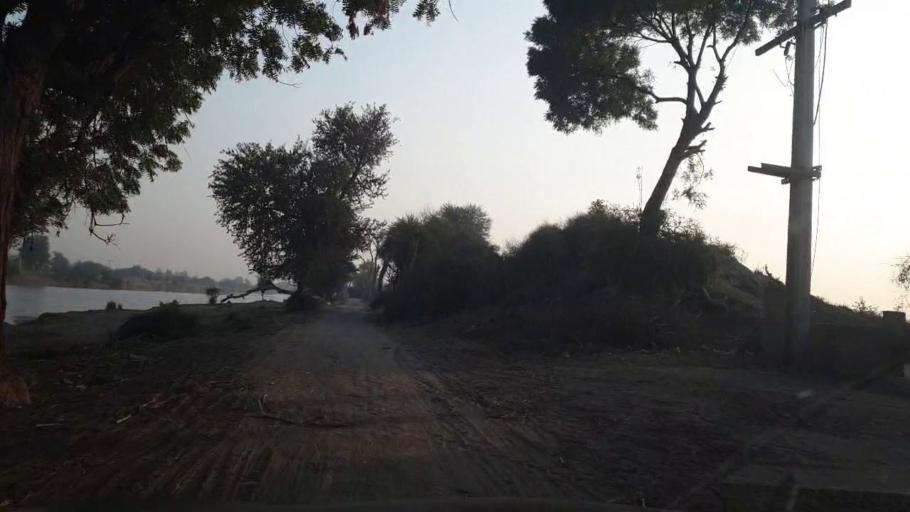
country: PK
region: Sindh
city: Ubauro
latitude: 28.3081
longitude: 69.7898
